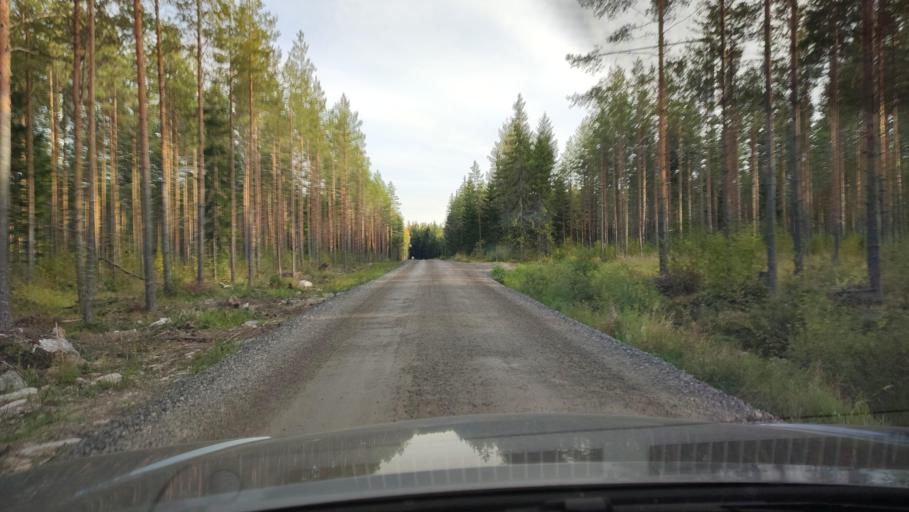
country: FI
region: Southern Ostrobothnia
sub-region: Suupohja
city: Karijoki
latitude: 62.1704
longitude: 21.5937
